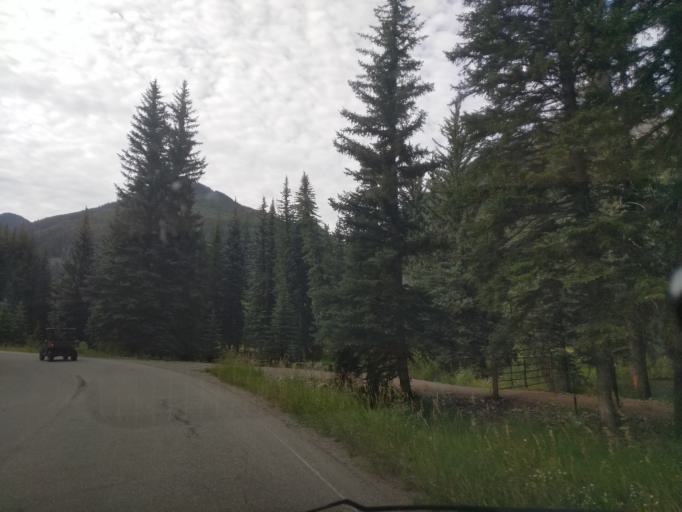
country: US
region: Colorado
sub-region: Gunnison County
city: Crested Butte
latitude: 39.0776
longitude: -107.2251
